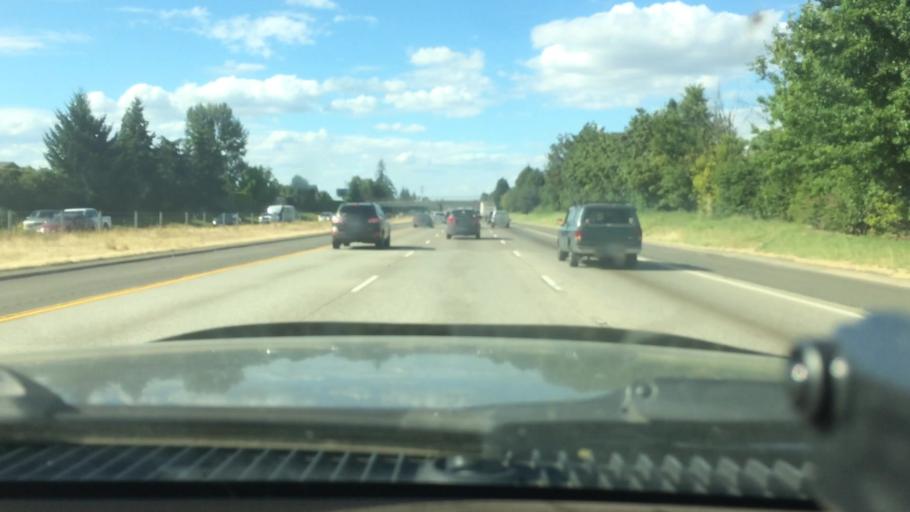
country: US
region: Oregon
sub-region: Marion County
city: Four Corners
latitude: 44.9361
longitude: -122.9902
